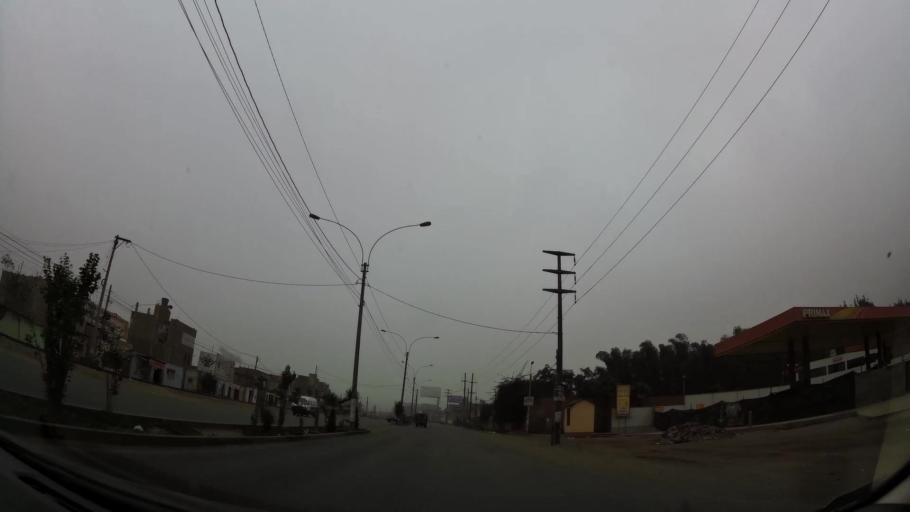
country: PE
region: Lima
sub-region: Lima
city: Santa Maria
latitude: -12.0062
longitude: -76.8490
